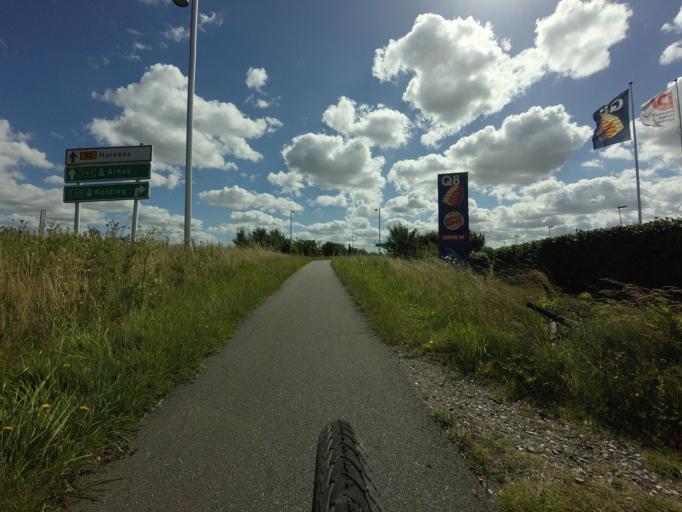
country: DK
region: Central Jutland
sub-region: Horsens Kommune
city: Horsens
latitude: 55.8864
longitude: 9.7880
